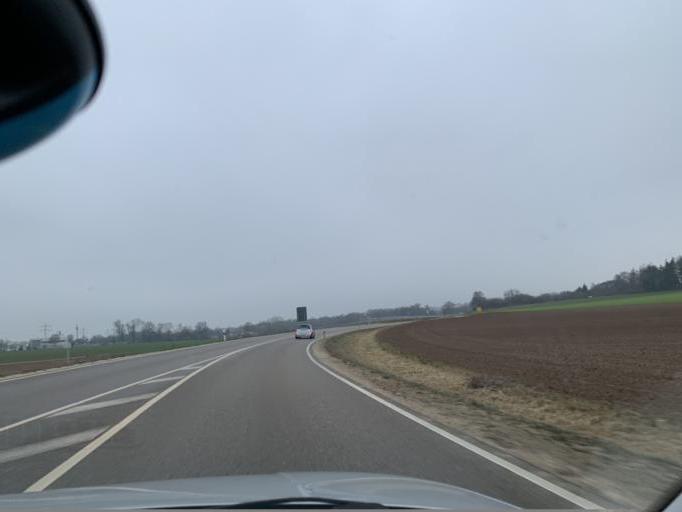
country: DE
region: Bavaria
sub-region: Upper Bavaria
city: Hepberg
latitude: 48.8111
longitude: 11.4776
